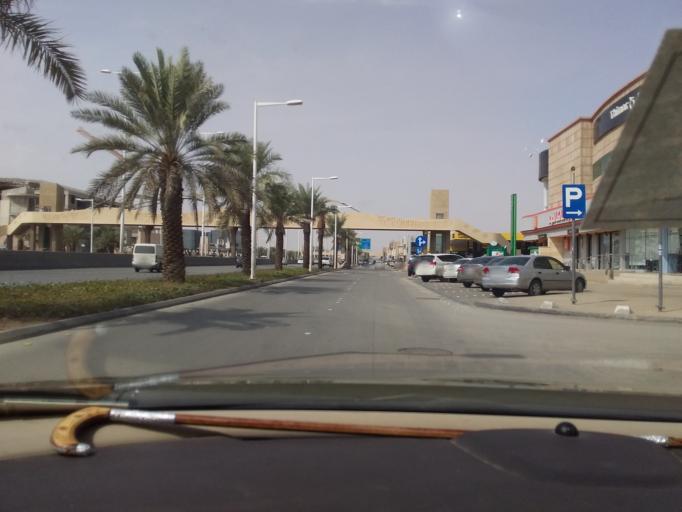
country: SA
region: Ar Riyad
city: Riyadh
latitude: 24.7360
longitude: 46.7075
